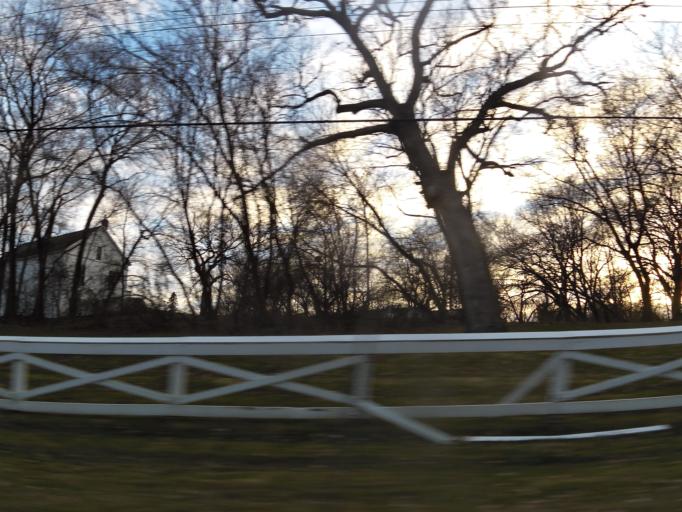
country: US
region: Minnesota
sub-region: Washington County
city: Dellwood
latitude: 45.0922
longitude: -92.9765
